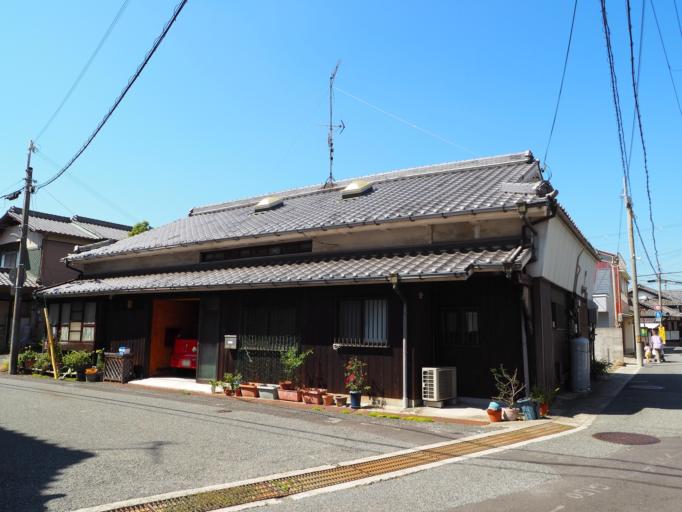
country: JP
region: Hyogo
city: Tatsunocho-tominaga
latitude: 34.7838
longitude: 134.5878
